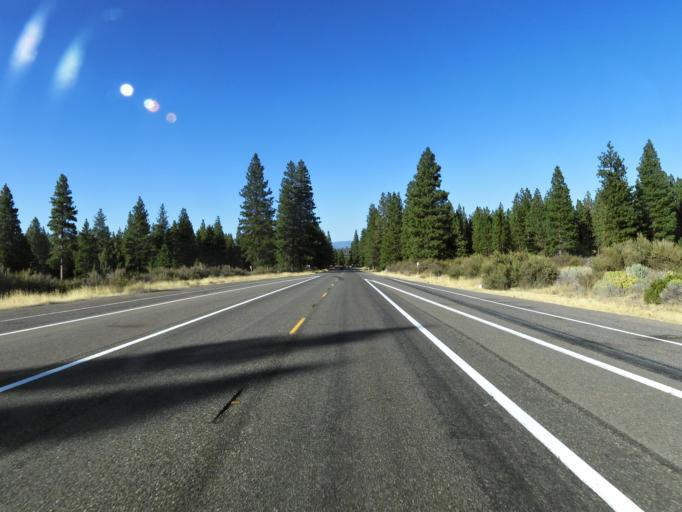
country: US
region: California
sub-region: Siskiyou County
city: Weed
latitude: 41.4540
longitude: -122.3599
